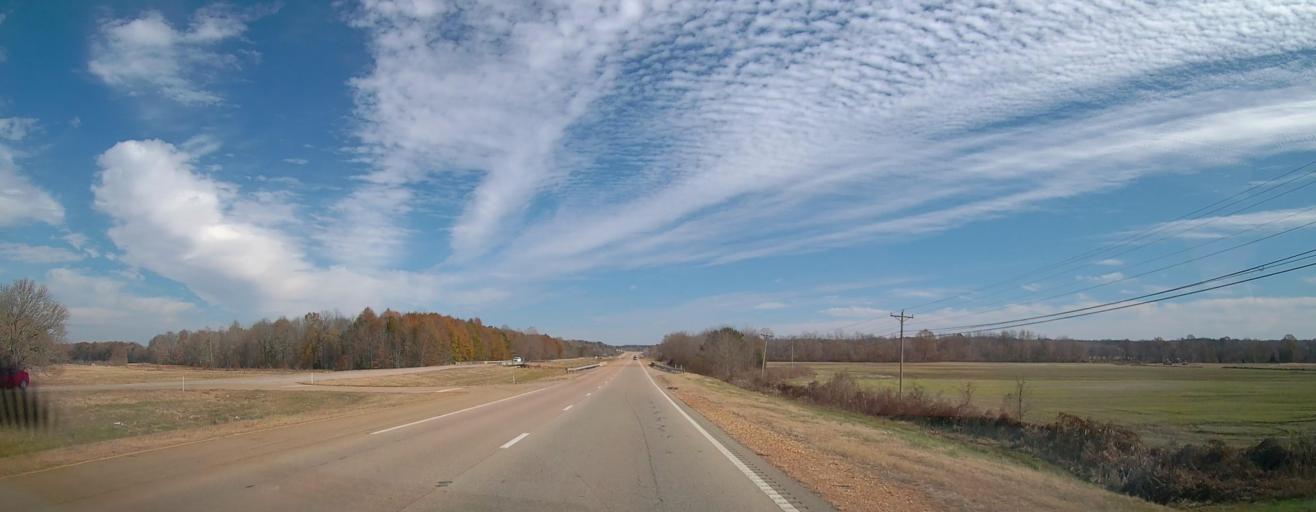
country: US
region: Mississippi
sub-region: Tippah County
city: Ripley
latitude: 34.9522
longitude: -88.8839
